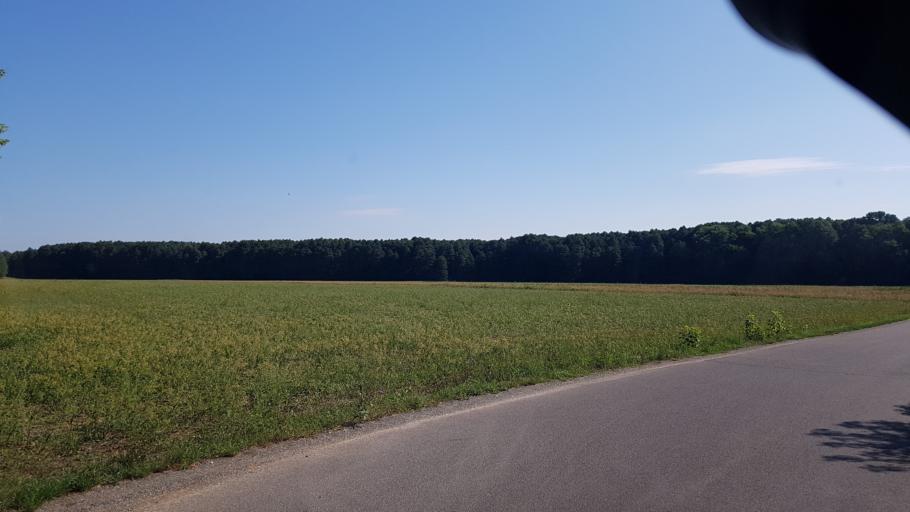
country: DE
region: Brandenburg
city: Vetschau
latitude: 51.7579
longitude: 14.0427
